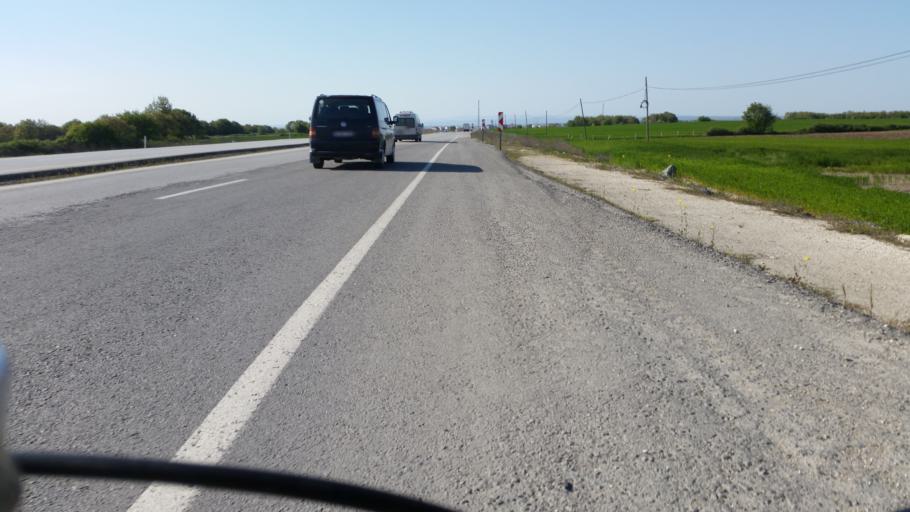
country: TR
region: Tekirdag
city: Cerkezkoey
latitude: 41.3440
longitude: 27.9626
